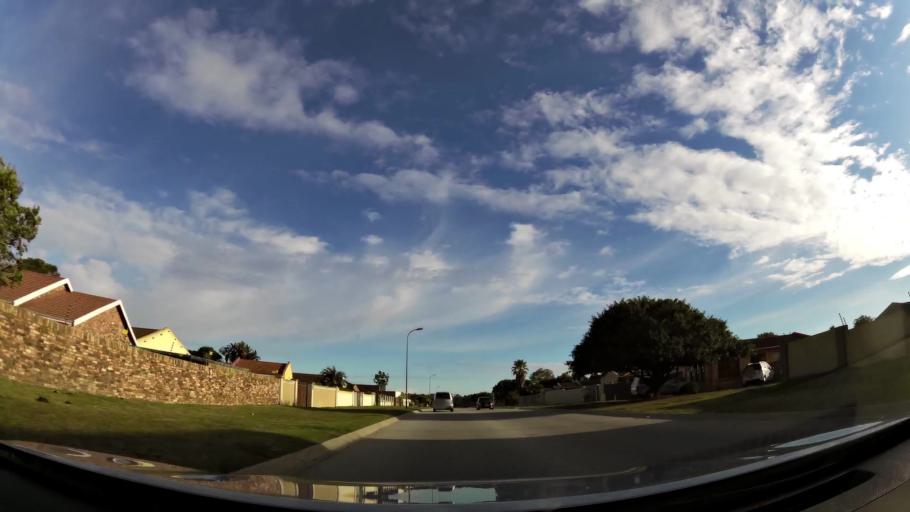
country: ZA
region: Eastern Cape
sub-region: Nelson Mandela Bay Metropolitan Municipality
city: Port Elizabeth
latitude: -33.9598
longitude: 25.4786
